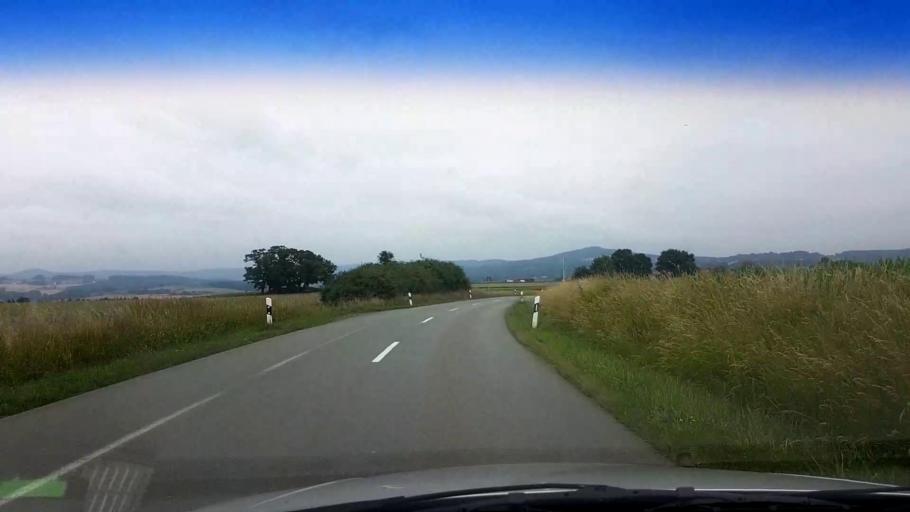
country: DE
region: Bavaria
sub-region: Upper Franconia
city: Mainleus
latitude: 50.0921
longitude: 11.3498
